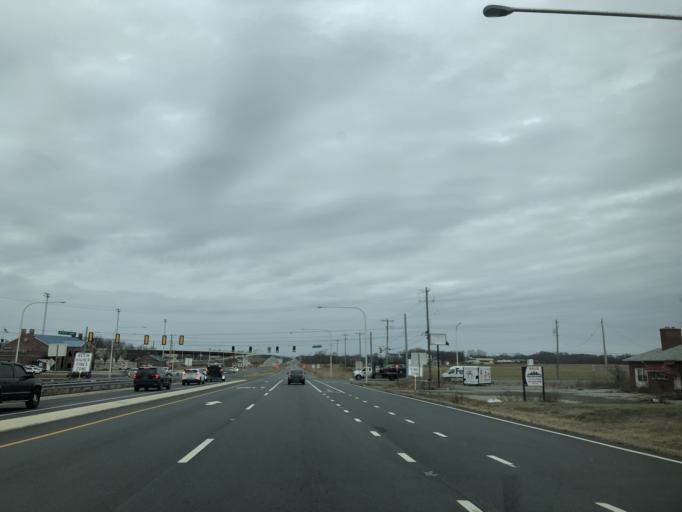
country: US
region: Delaware
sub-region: New Castle County
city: Delaware City
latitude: 39.5237
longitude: -75.6489
